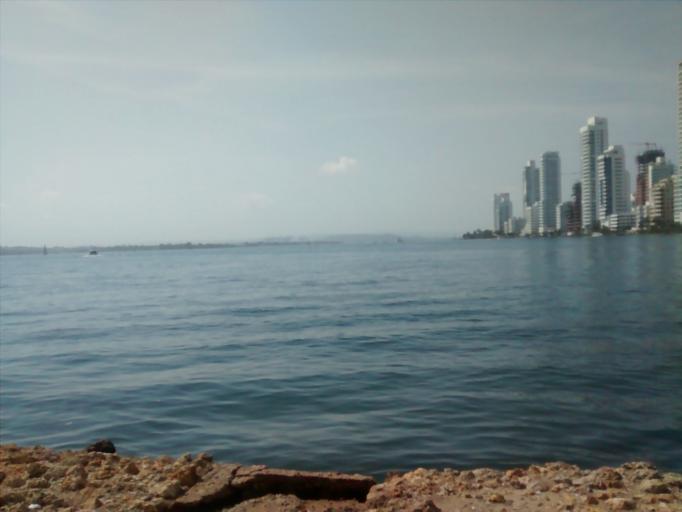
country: CO
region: Bolivar
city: Cartagena
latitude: 10.3996
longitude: -75.5537
